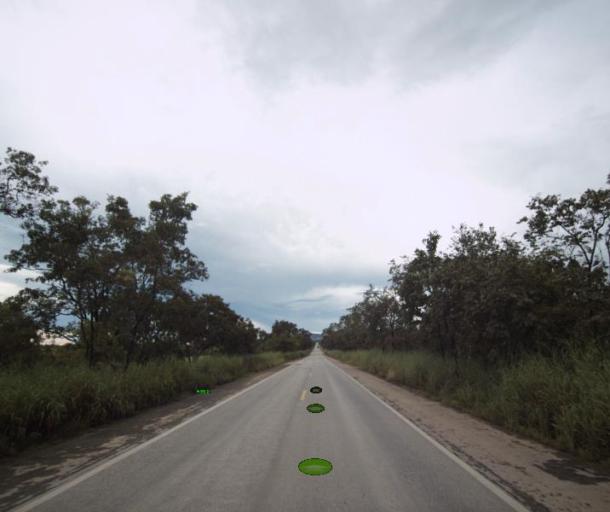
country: BR
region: Goias
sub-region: Porangatu
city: Porangatu
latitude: -13.5617
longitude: -49.0575
